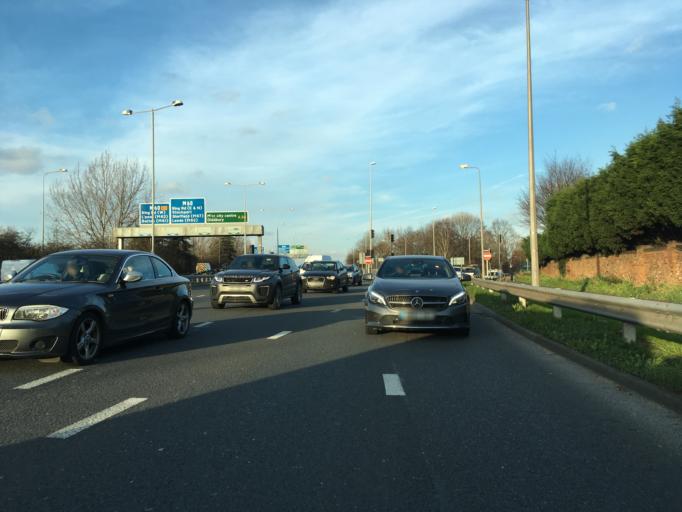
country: GB
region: England
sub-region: Manchester
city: Didsbury
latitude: 53.3945
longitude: -2.2264
